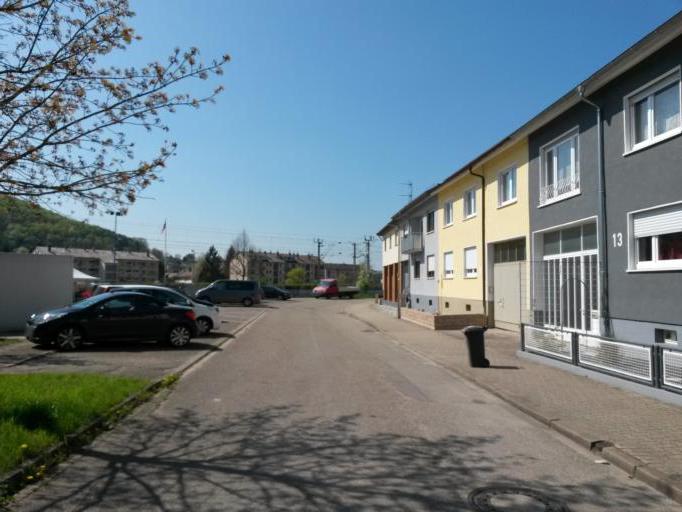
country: DE
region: Baden-Wuerttemberg
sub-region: Karlsruhe Region
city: Joehlingen
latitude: 49.0015
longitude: 8.5379
